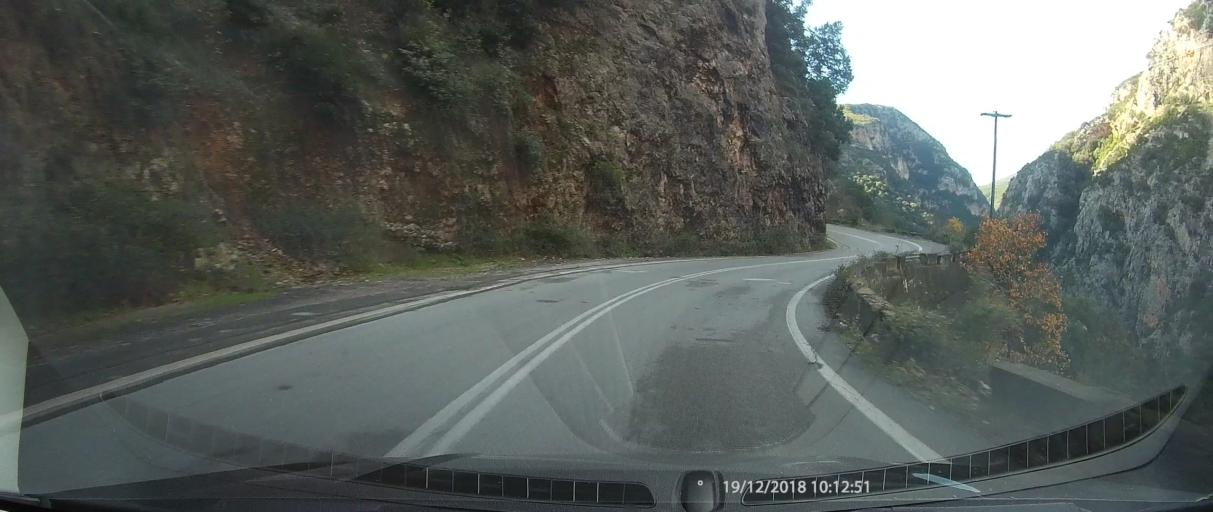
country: GR
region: Peloponnese
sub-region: Nomos Messinias
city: Kalamata
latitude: 37.0888
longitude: 22.1639
